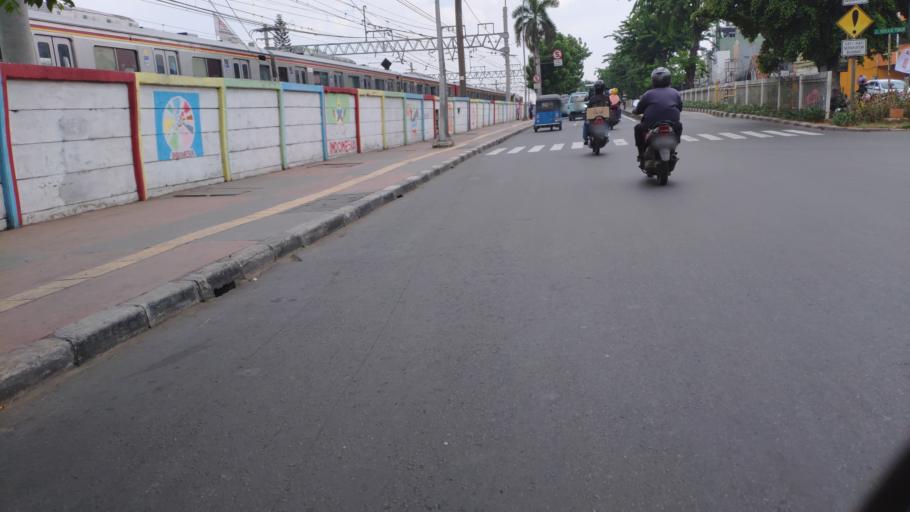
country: ID
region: Jakarta Raya
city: Jakarta
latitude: -6.2150
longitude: 106.8754
